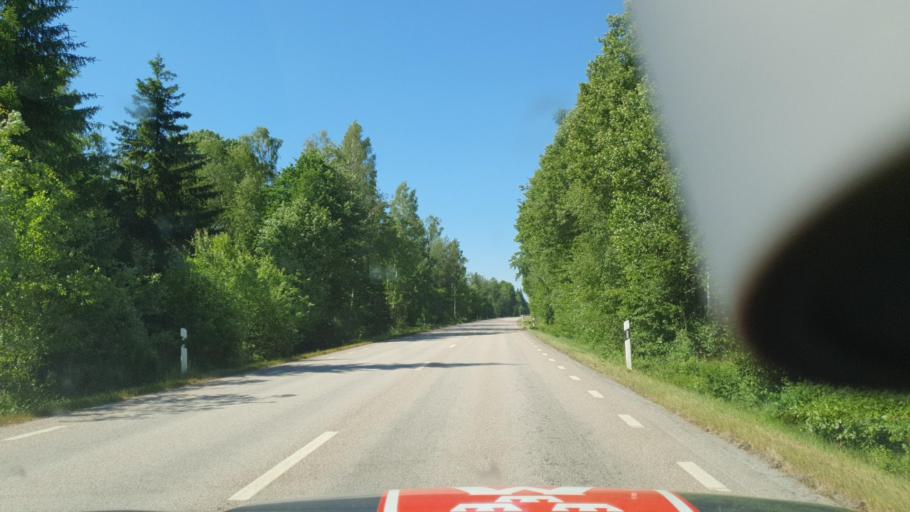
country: SE
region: Kalmar
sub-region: Emmaboda Kommun
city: Emmaboda
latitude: 56.5945
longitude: 15.5710
